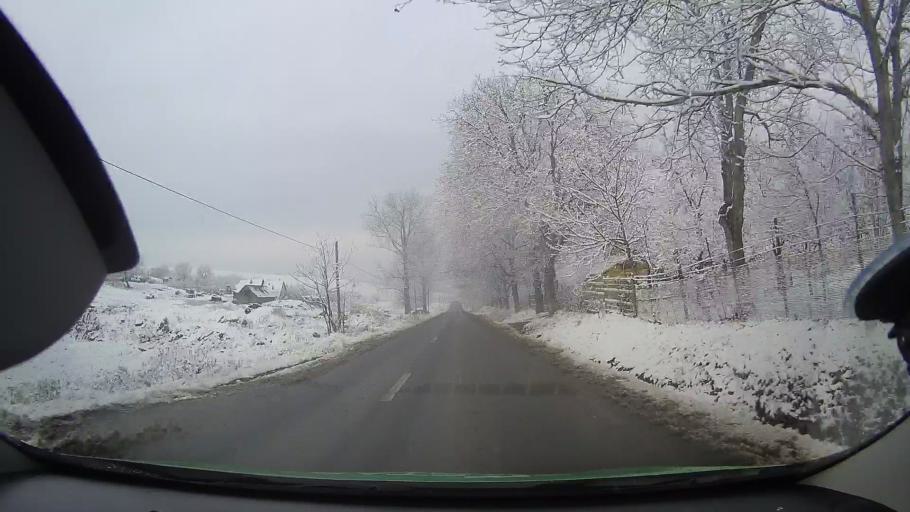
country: RO
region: Mures
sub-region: Comuna Atintis
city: Atintis
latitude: 46.4465
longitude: 24.0888
